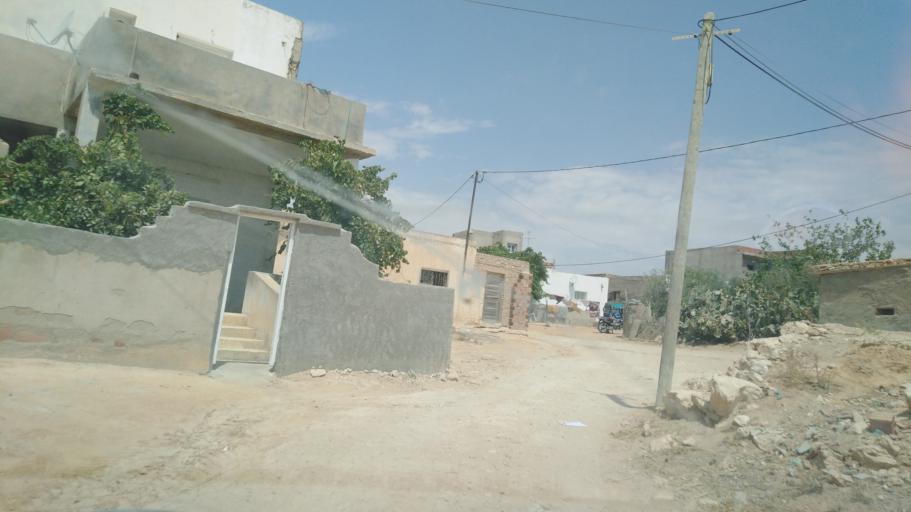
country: TN
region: Safaqis
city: Sfax
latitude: 34.7416
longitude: 10.5614
